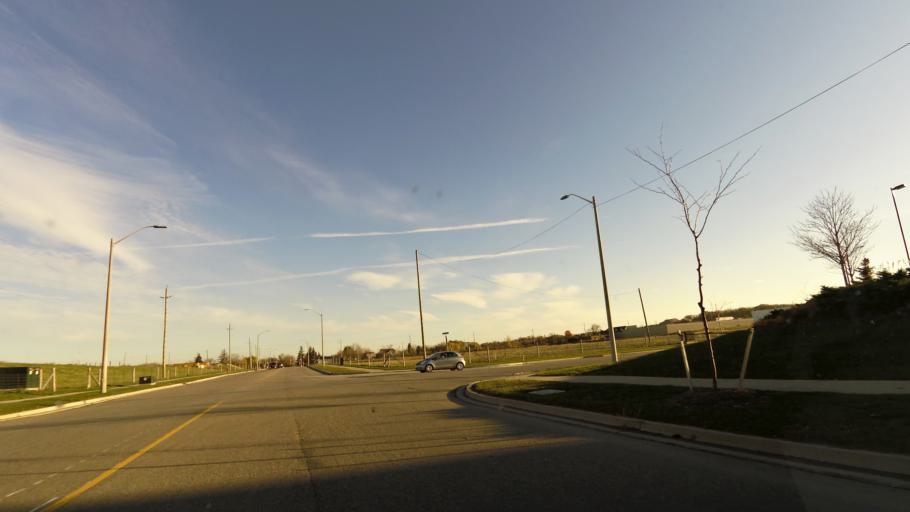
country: CA
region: Ontario
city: Mississauga
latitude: 43.5868
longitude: -79.7299
